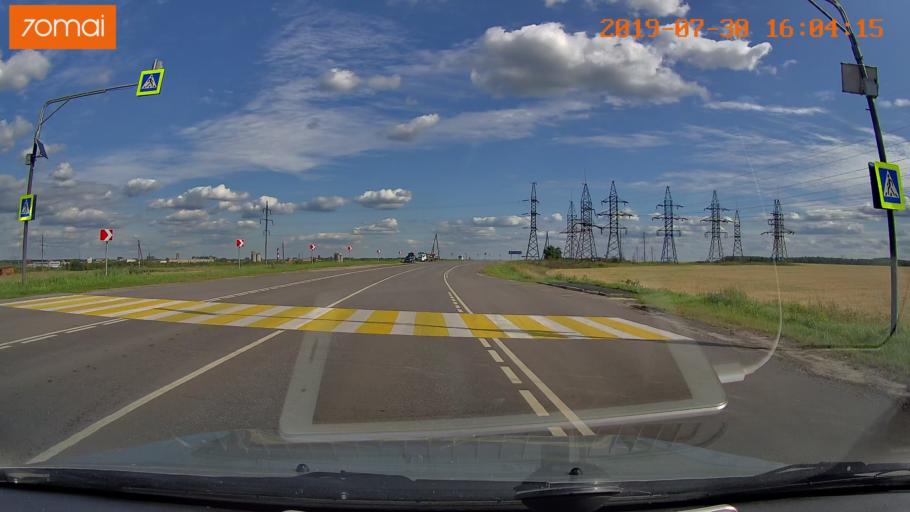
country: RU
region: Moskovskaya
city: Lopatinskiy
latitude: 55.2829
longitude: 38.7051
